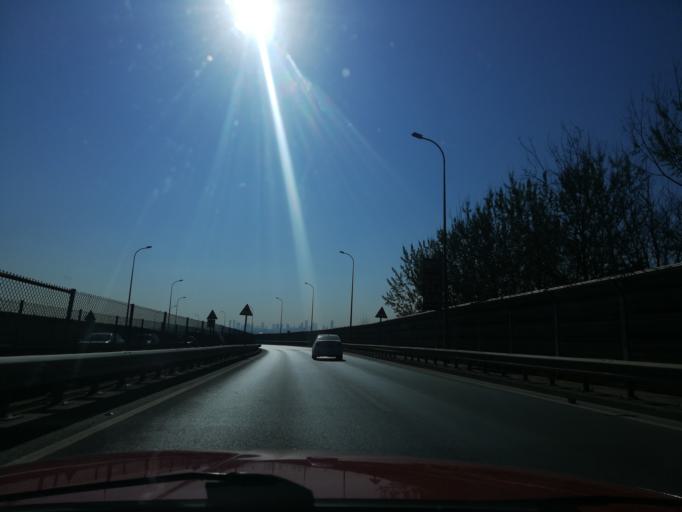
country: TR
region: Istanbul
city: Mahmut Sevket Pasa
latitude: 41.1178
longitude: 29.1222
